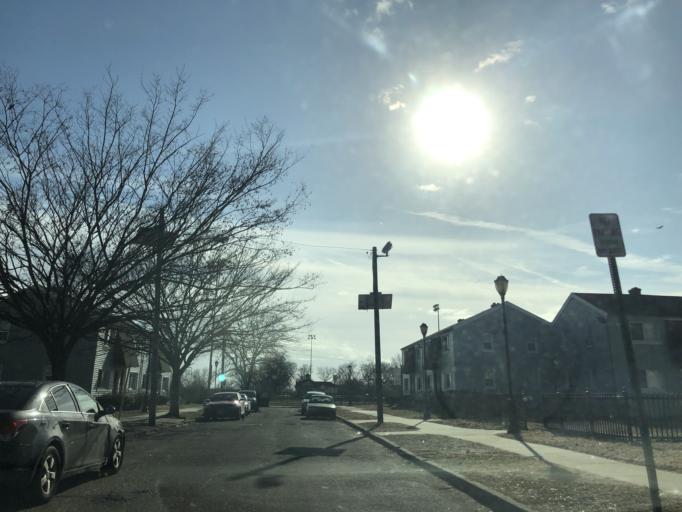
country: US
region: New Jersey
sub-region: Camden County
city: Camden
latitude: 39.9268
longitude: -75.1144
